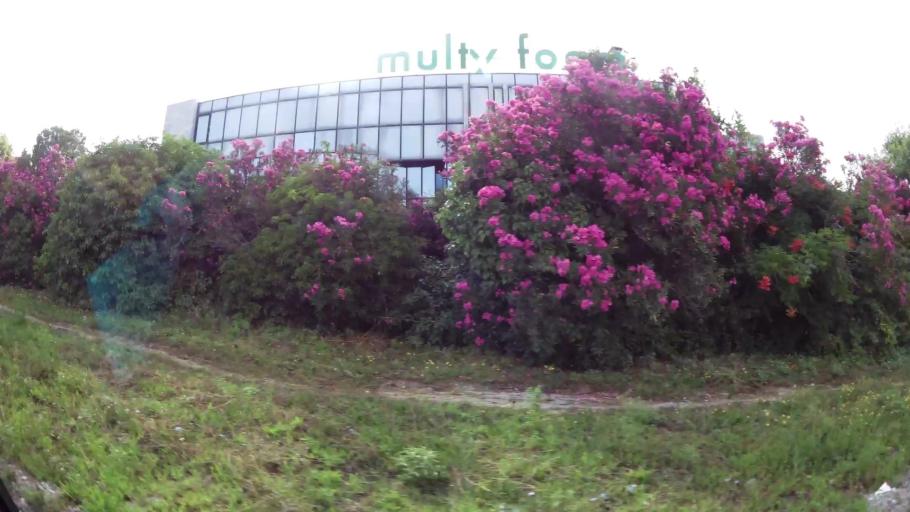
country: GR
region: Central Macedonia
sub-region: Nomos Thessalonikis
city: Thermi
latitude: 40.5559
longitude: 23.0194
